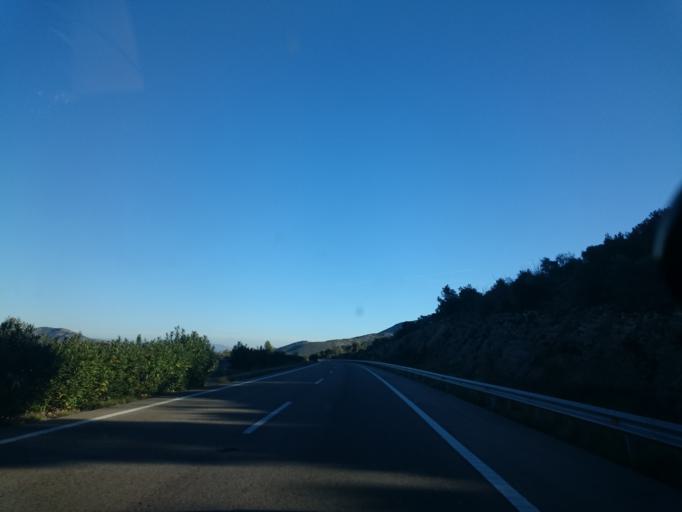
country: ES
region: Valencia
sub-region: Provincia de Castello
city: Santa Magdalena de Pulpis
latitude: 40.3559
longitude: 0.3146
